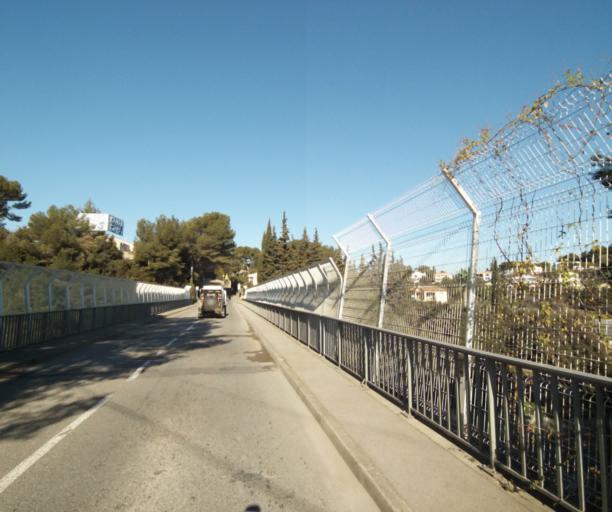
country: FR
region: Provence-Alpes-Cote d'Azur
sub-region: Departement des Alpes-Maritimes
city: Biot
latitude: 43.6051
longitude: 7.0906
